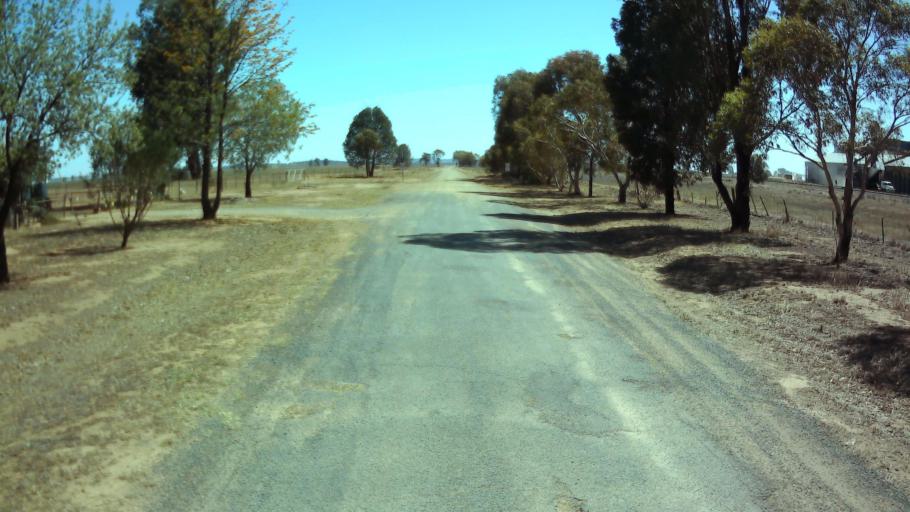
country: AU
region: New South Wales
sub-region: Weddin
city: Grenfell
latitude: -33.8396
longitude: 147.7413
